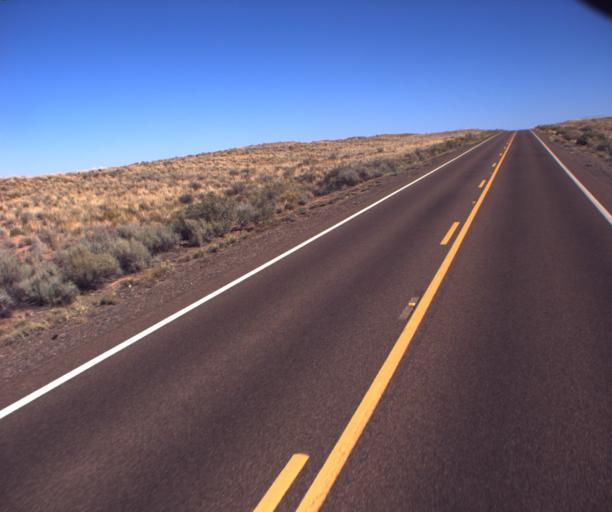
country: US
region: Arizona
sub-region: Navajo County
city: Winslow
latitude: 35.0667
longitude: -110.5768
